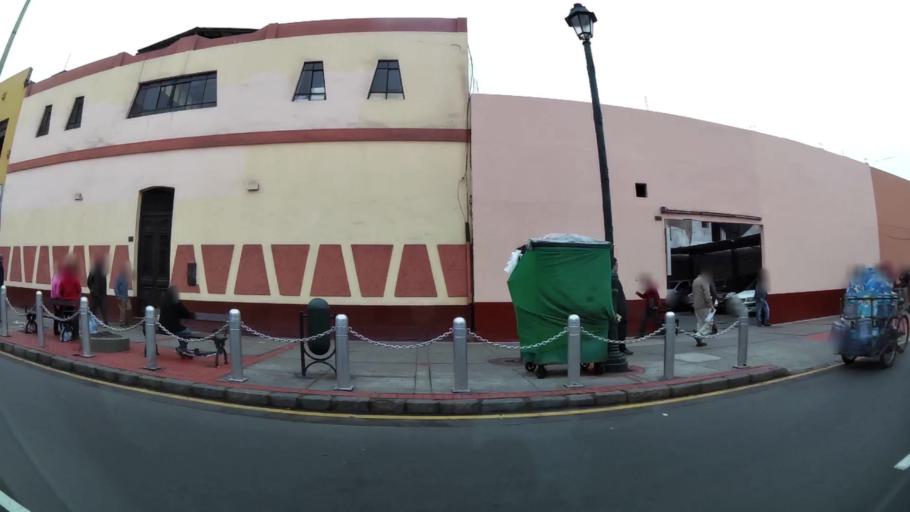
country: PE
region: Lima
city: Lima
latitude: -12.0509
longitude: -77.0317
